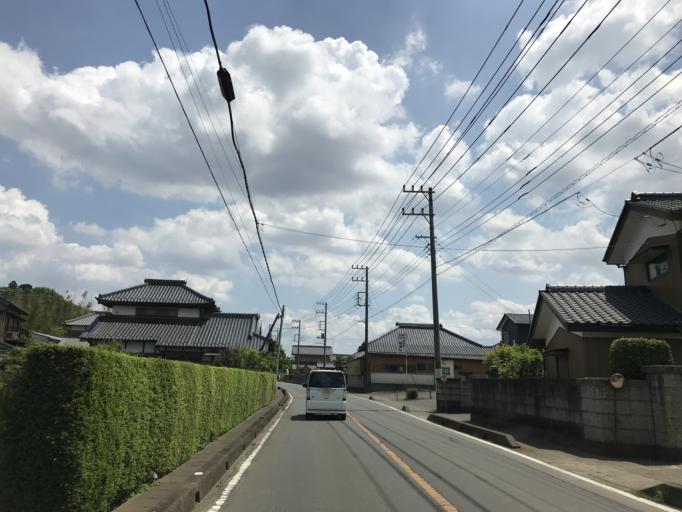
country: JP
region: Ibaraki
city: Mitsukaido
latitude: 36.0537
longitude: 140.0383
